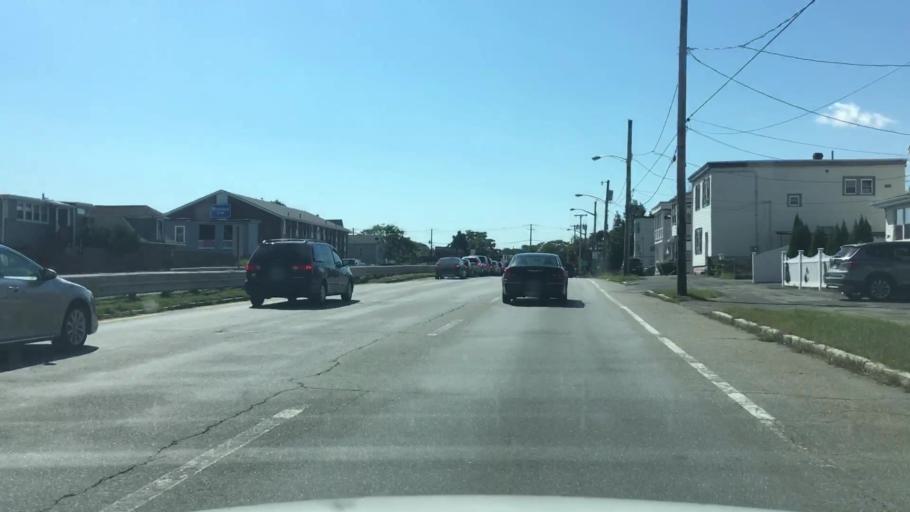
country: US
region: Massachusetts
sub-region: Suffolk County
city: Revere
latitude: 42.4184
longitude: -71.0024
